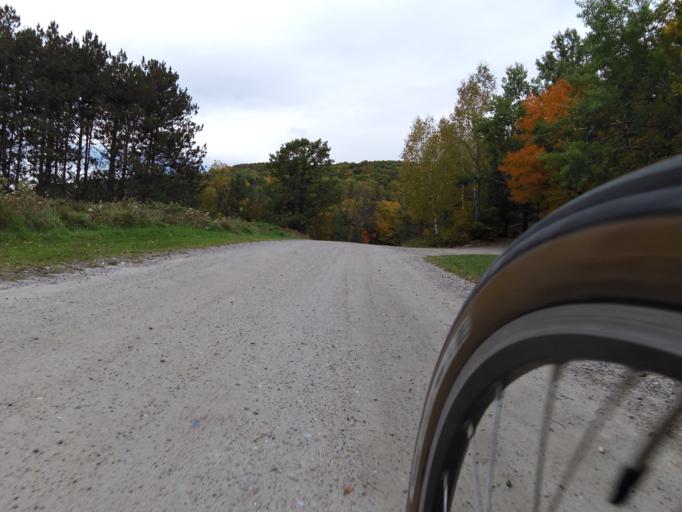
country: CA
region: Quebec
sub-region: Outaouais
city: Wakefield
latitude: 45.6035
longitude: -76.0212
